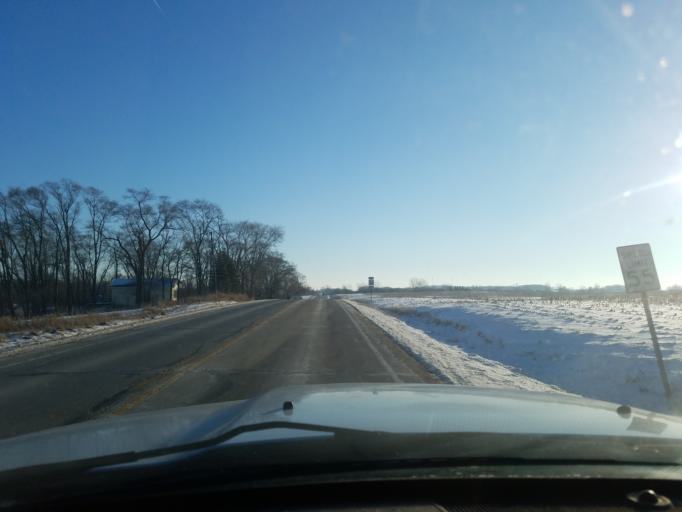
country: US
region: Indiana
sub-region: Noble County
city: Ligonier
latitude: 41.4523
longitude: -85.5652
